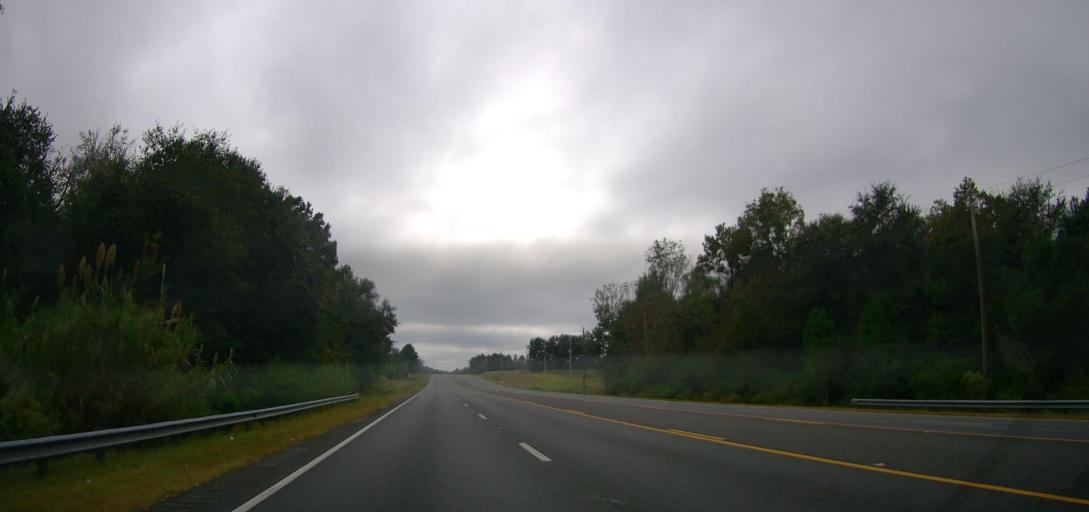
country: US
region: Georgia
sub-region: Thomas County
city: Thomasville
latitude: 30.9347
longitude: -83.9107
